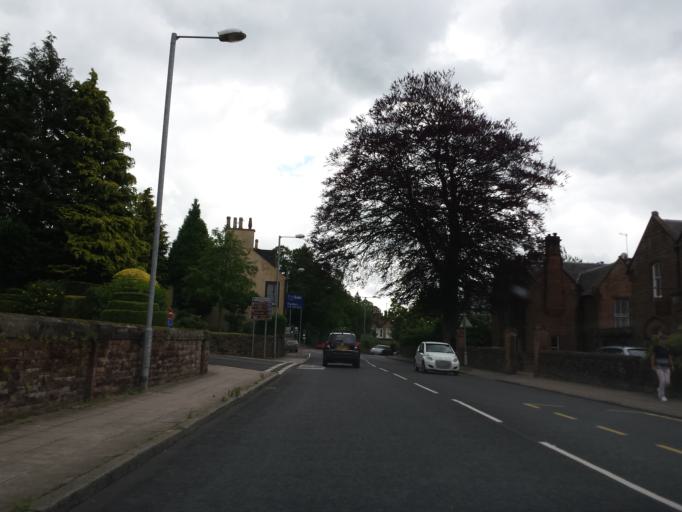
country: GB
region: Scotland
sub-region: Dumfries and Galloway
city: Dumfries
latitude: 55.0618
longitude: -3.6036
